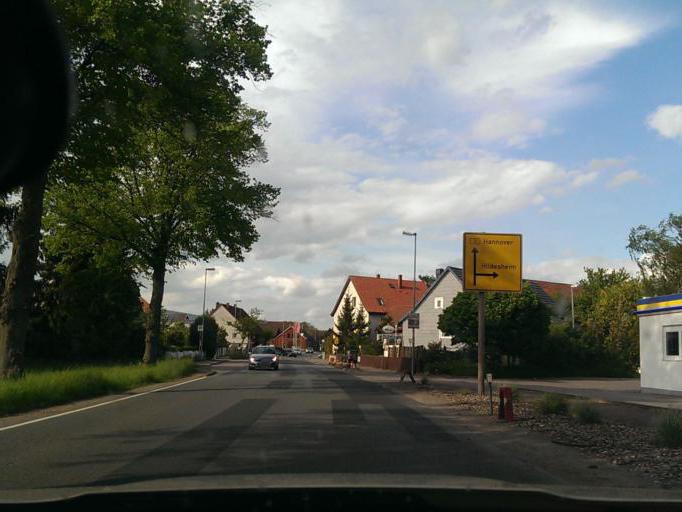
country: DE
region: Lower Saxony
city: Elze
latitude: 52.1499
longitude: 9.7379
